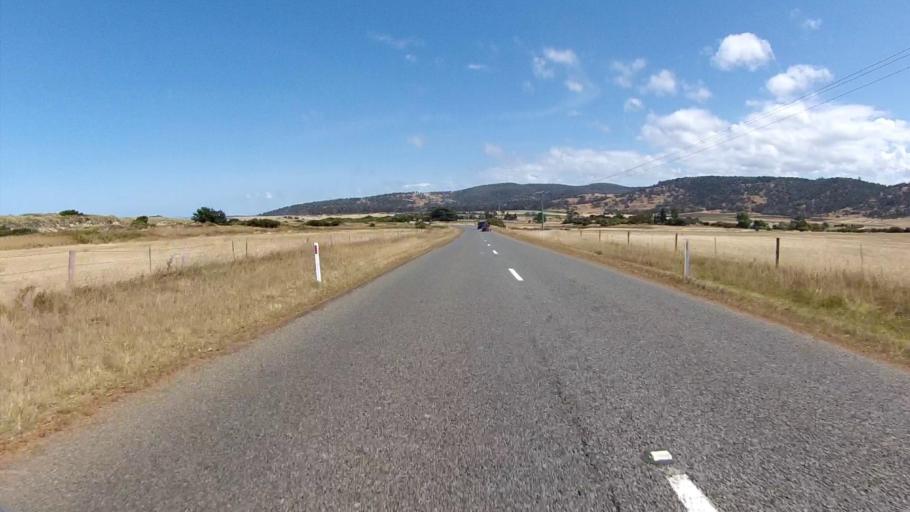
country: AU
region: Tasmania
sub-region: Sorell
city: Sorell
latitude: -42.1964
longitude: 148.0523
